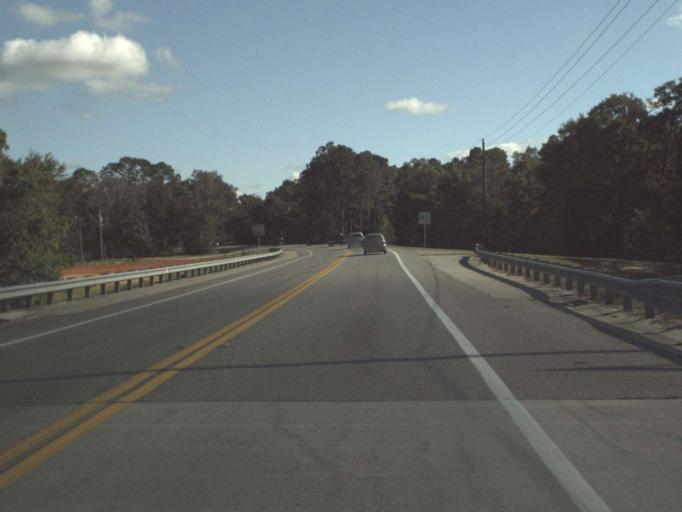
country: US
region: Florida
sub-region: Gulf County
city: Wewahitchka
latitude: 30.1303
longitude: -85.2064
